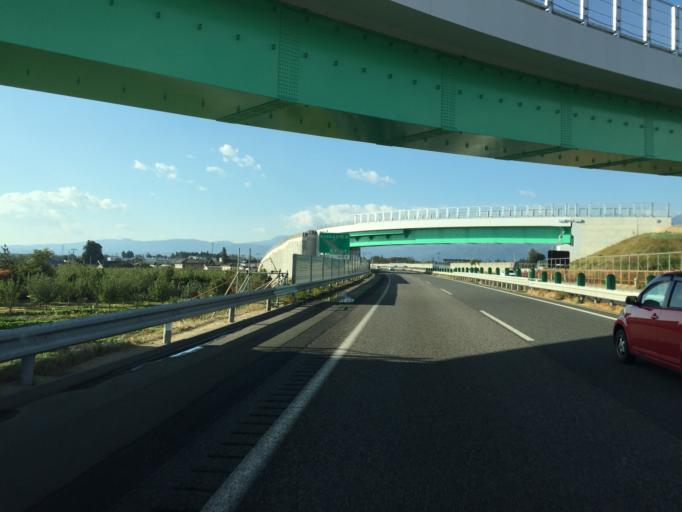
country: JP
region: Fukushima
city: Fukushima-shi
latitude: 37.7894
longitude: 140.4181
